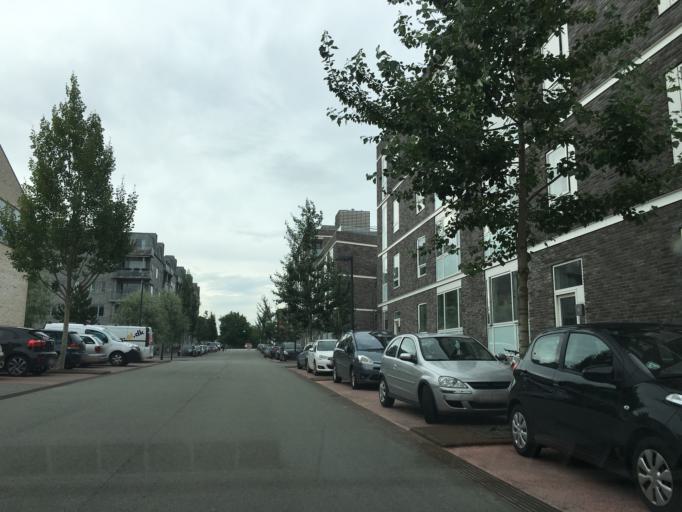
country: DK
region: Capital Region
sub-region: Frederiksberg Kommune
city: Frederiksberg
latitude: 55.6568
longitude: 12.5097
